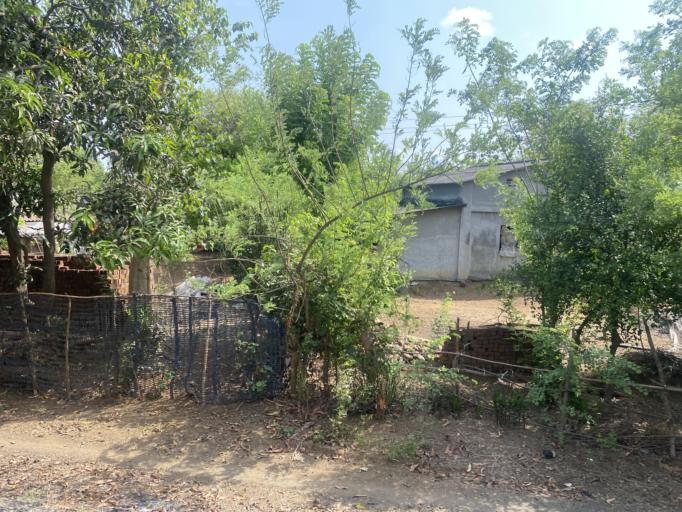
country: IN
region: Daman and Diu
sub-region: Daman District
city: Daman
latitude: 20.3303
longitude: 72.8120
